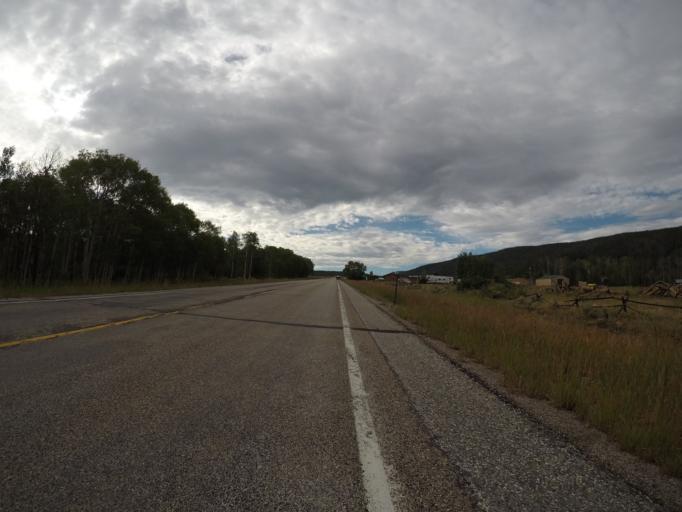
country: US
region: Wyoming
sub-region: Carbon County
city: Saratoga
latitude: 41.3545
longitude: -106.5368
